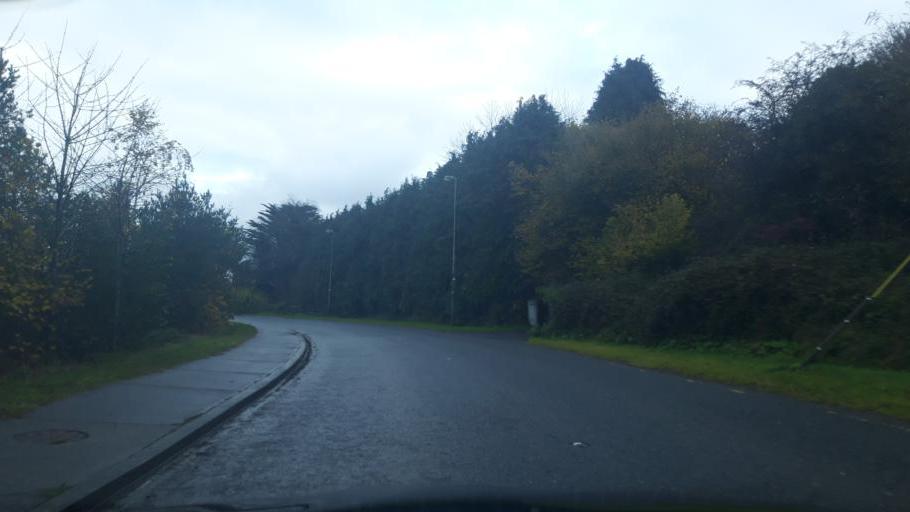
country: IE
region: Leinster
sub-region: Wicklow
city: Kilmacanoge
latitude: 53.1450
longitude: -6.1225
